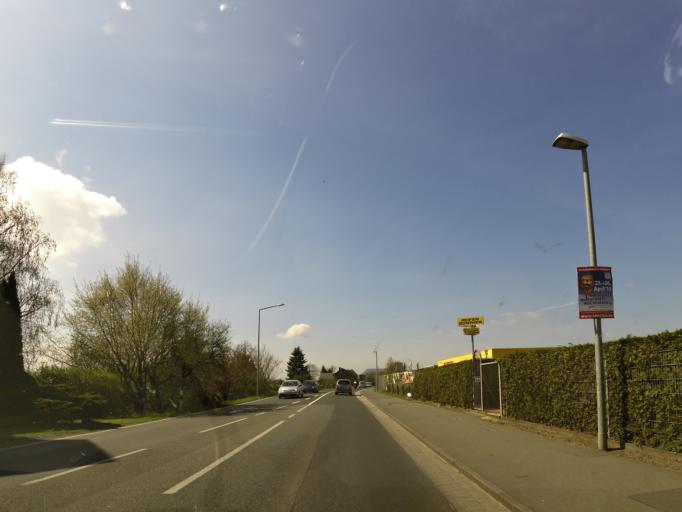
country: DE
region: Lower Saxony
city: Wunstorf
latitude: 52.4284
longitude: 9.4148
